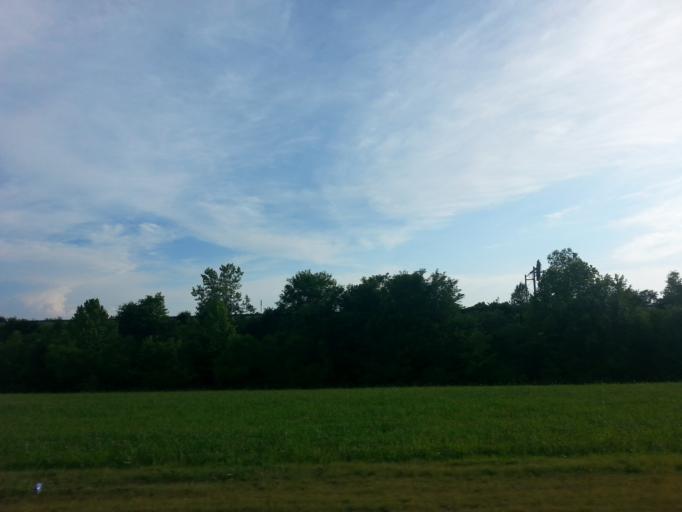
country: US
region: Tennessee
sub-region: Knox County
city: Farragut
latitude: 35.9164
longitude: -84.1229
